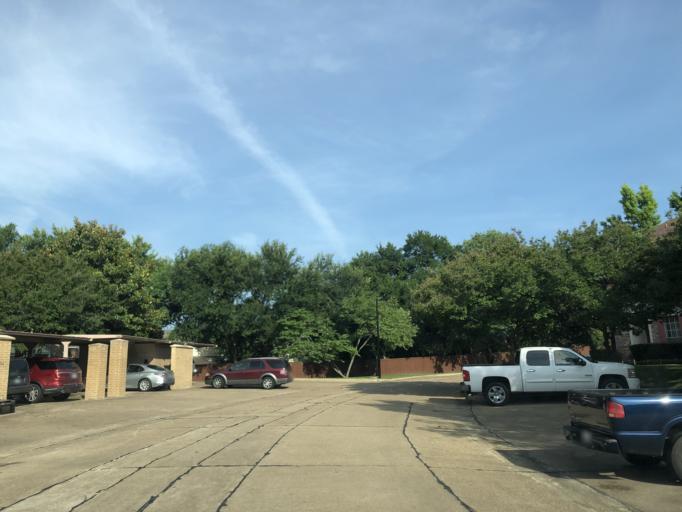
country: US
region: Texas
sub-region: Dallas County
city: Sunnyvale
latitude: 32.8409
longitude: -96.6120
